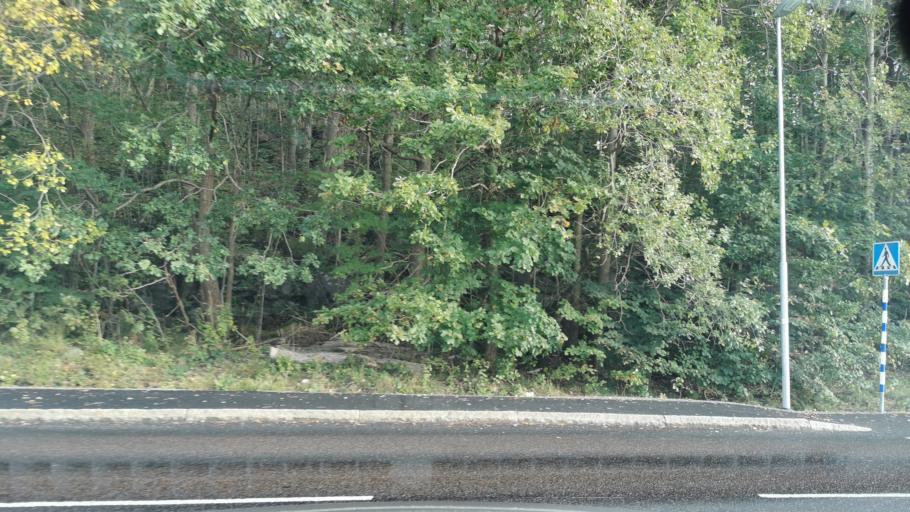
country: SE
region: Vaestra Goetaland
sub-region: Partille Kommun
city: Partille
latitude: 57.7191
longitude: 12.0822
